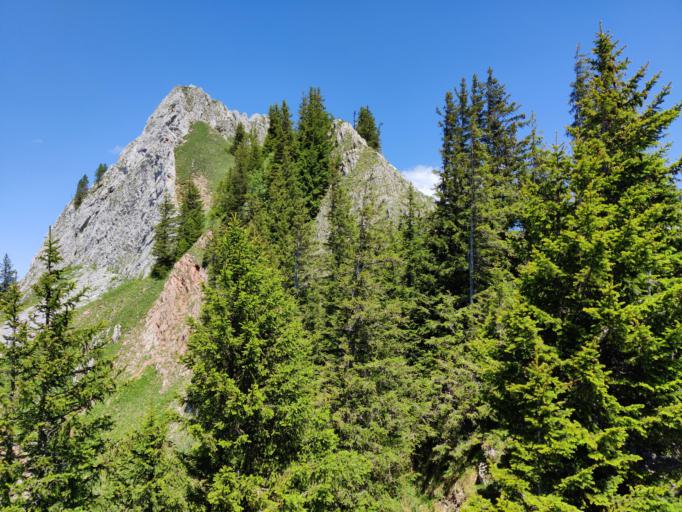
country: CH
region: Bern
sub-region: Obersimmental-Saanen District
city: Saanen
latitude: 46.5685
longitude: 7.2648
